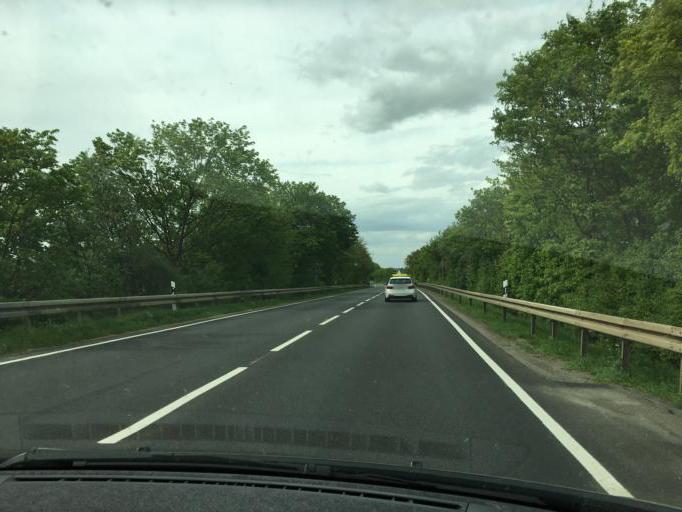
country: DE
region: North Rhine-Westphalia
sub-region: Regierungsbezirk Koln
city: Euskirchen
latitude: 50.6840
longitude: 6.7488
